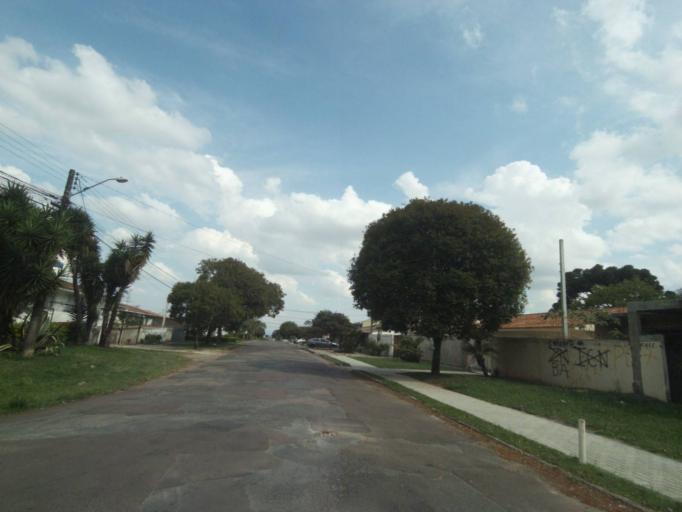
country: BR
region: Parana
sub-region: Pinhais
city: Pinhais
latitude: -25.4103
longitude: -49.2086
